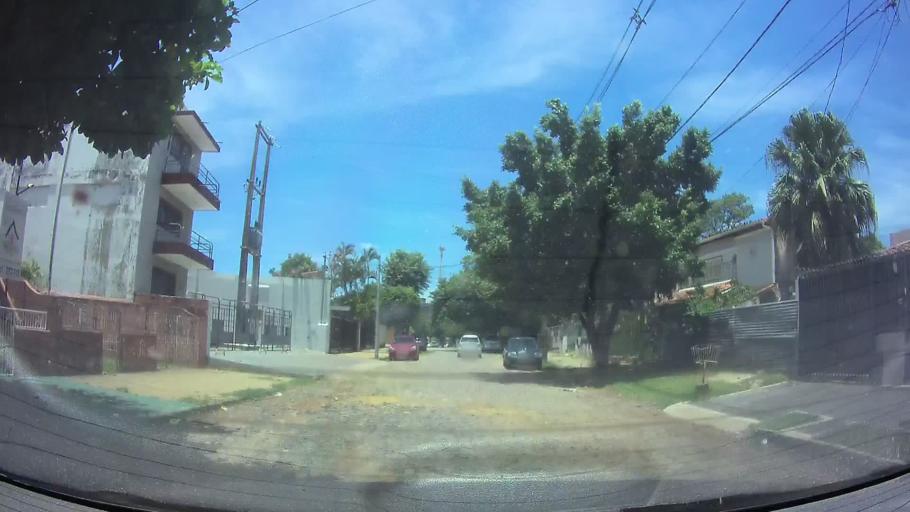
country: PY
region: Asuncion
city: Asuncion
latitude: -25.2710
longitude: -57.6004
